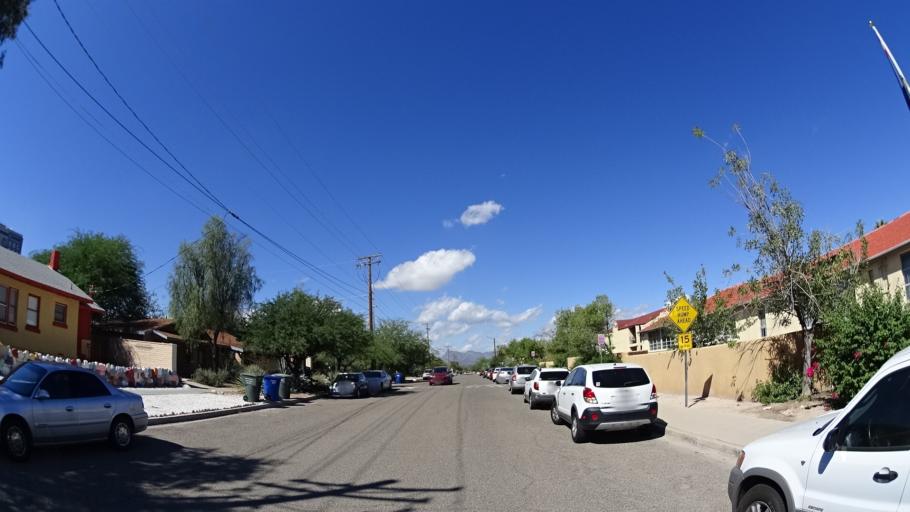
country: US
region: Arizona
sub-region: Pima County
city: Tucson
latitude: 32.2373
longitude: -110.9569
